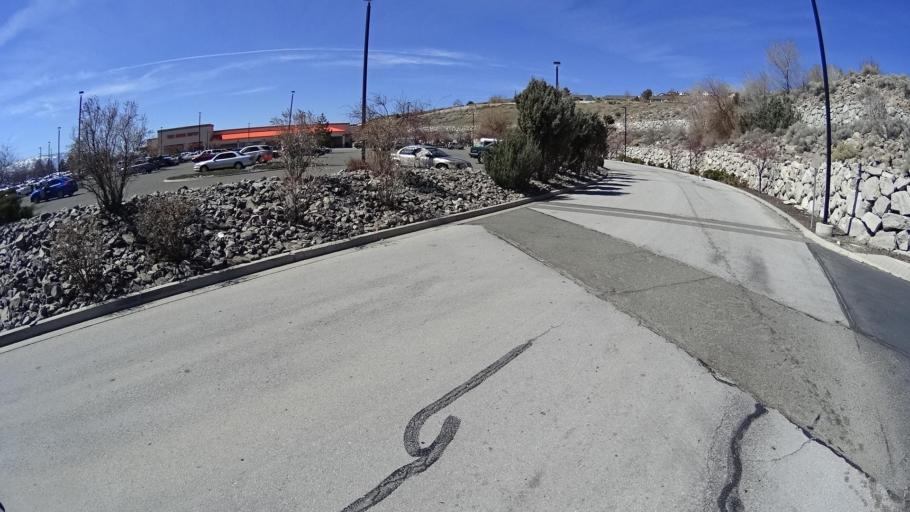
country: US
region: Nevada
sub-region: Washoe County
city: Sparks
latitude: 39.5579
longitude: -119.7825
